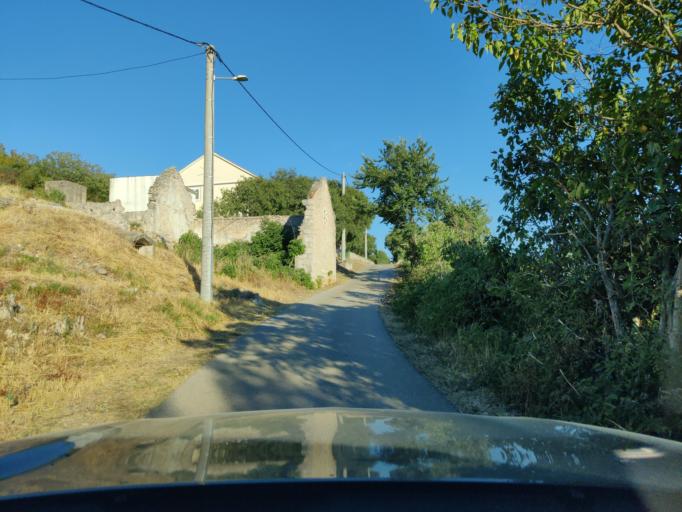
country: HR
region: Sibensko-Kniniska
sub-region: Grad Sibenik
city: Pirovac
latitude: 43.8628
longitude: 15.7175
